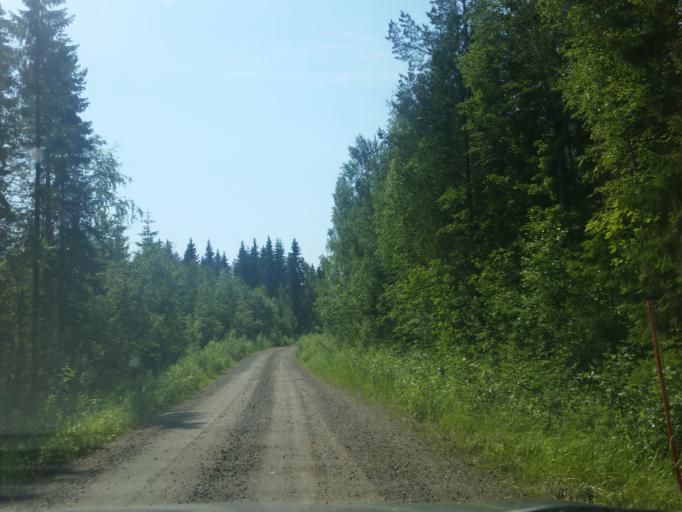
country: FI
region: Northern Savo
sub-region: Sisae-Savo
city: Tervo
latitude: 63.0895
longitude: 26.5834
